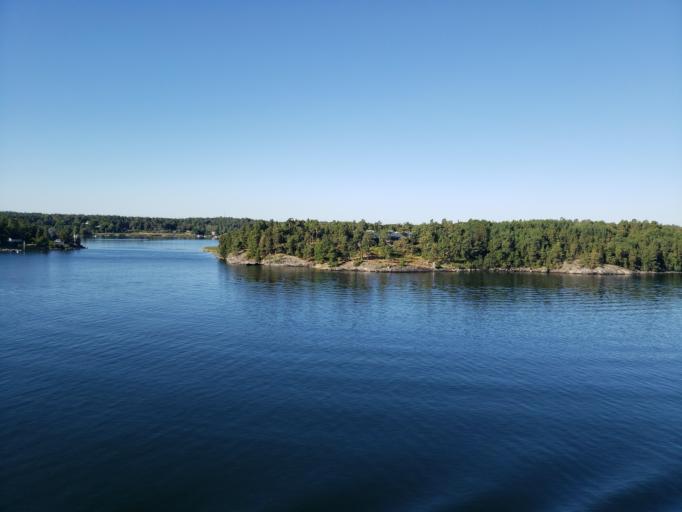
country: SE
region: Stockholm
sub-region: Vaxholms Kommun
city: Vaxholm
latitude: 59.4132
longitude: 18.4141
